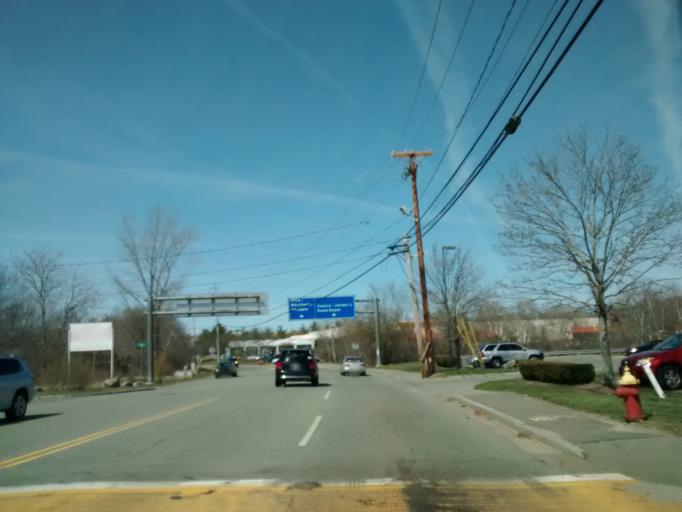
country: US
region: Massachusetts
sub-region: Norfolk County
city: Avon
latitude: 42.1288
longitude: -71.0667
